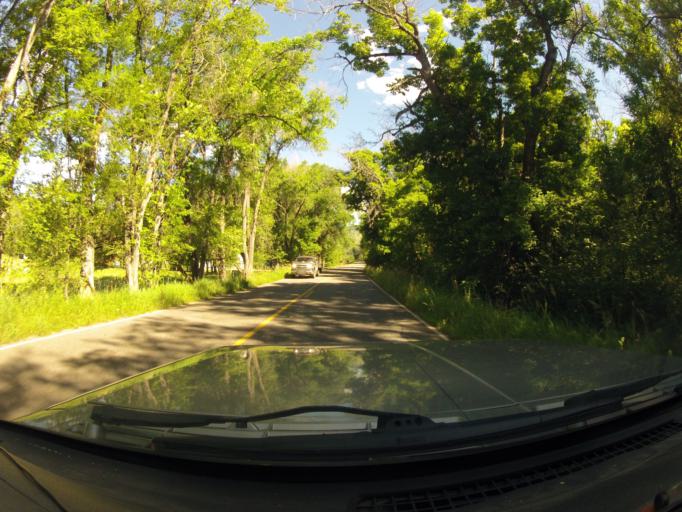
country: US
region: Colorado
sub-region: Larimer County
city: Laporte
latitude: 40.4890
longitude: -105.2167
